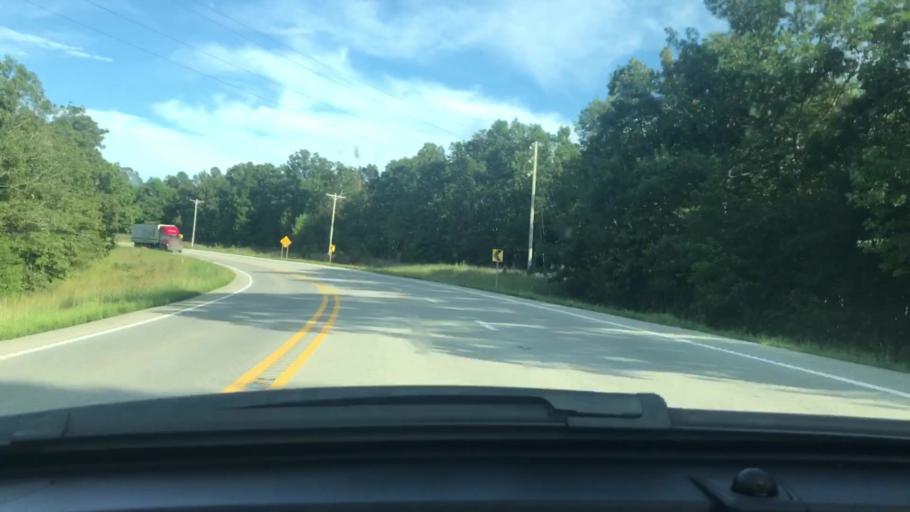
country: US
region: Arkansas
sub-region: Sharp County
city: Cherokee Village
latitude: 36.2741
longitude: -91.3211
